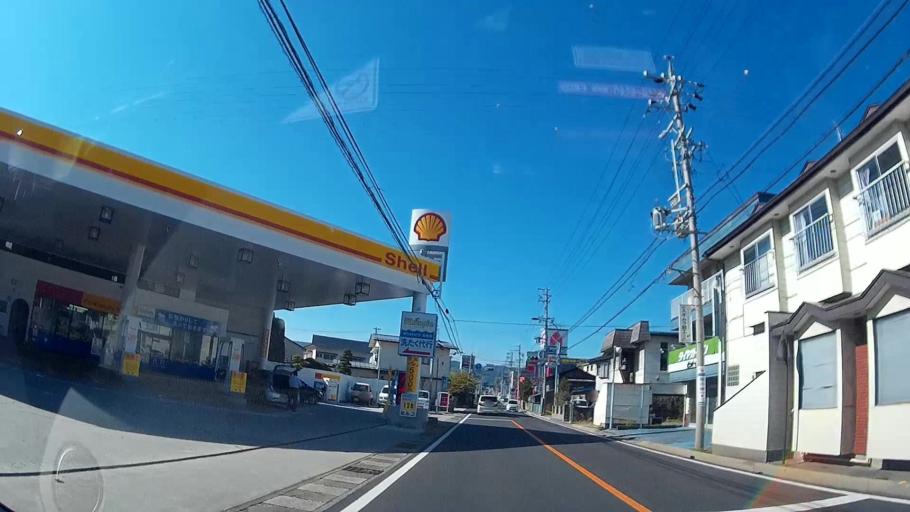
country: JP
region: Nagano
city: Okaya
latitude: 36.0766
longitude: 138.0730
